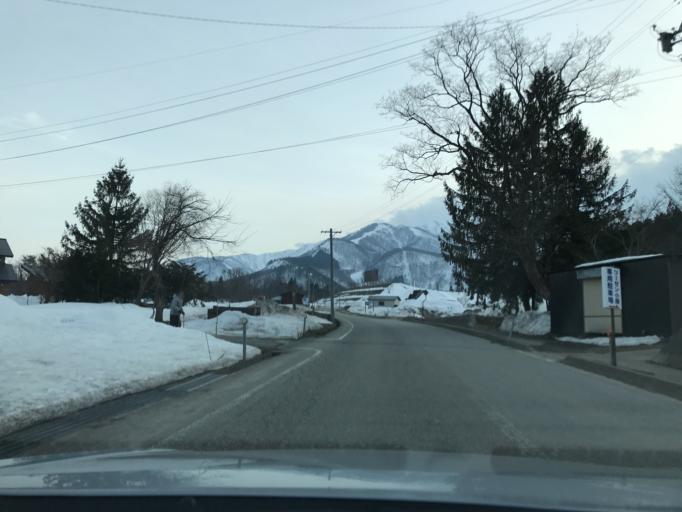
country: JP
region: Nagano
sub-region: Kitaazumi Gun
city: Hakuba
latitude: 36.6980
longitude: 137.8399
